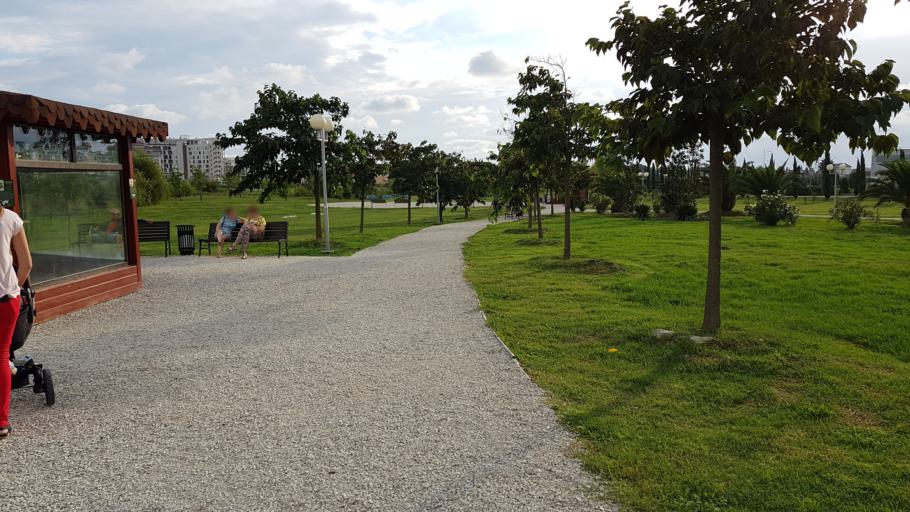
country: RU
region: Krasnodarskiy
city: Vysokoye
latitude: 43.3952
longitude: 39.9927
